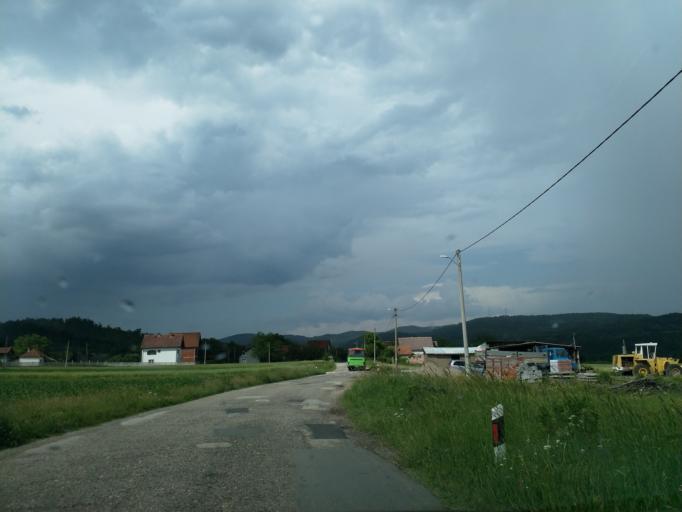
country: RS
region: Central Serbia
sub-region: Borski Okrug
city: Bor
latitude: 44.0019
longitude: 21.9795
